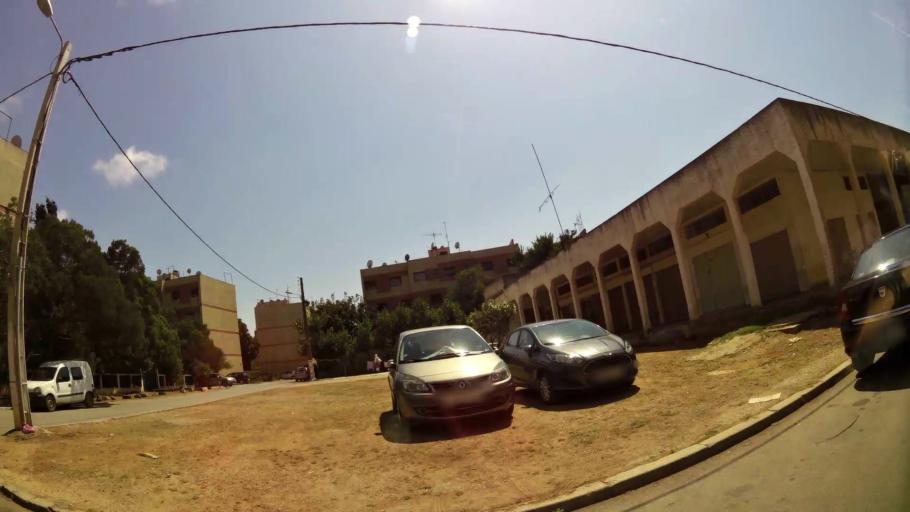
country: MA
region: Rabat-Sale-Zemmour-Zaer
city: Sale
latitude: 34.0424
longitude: -6.7904
